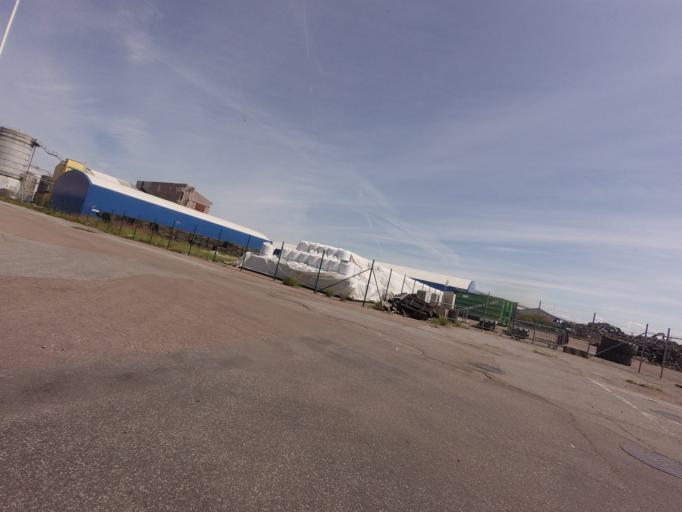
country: SE
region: Skane
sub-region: Landskrona
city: Landskrona
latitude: 55.8604
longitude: 12.8310
